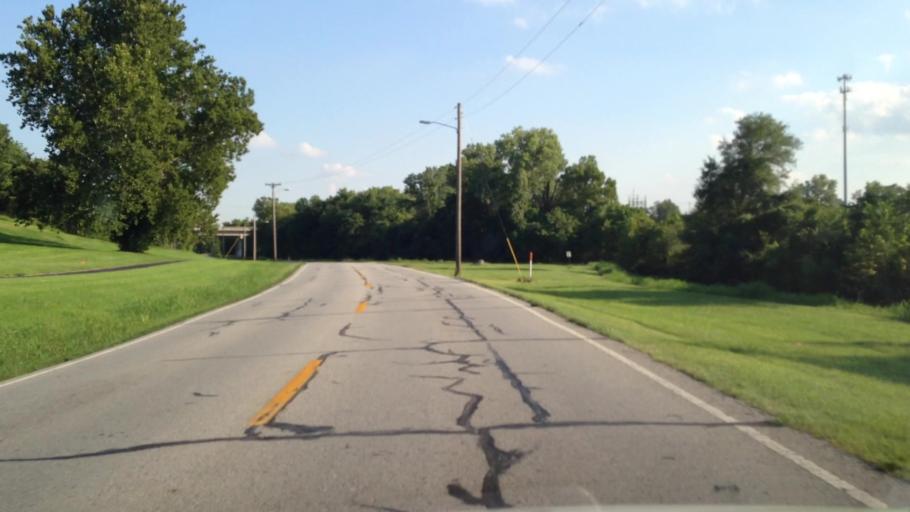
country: US
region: Missouri
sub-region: Jasper County
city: Joplin
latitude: 37.0941
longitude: -94.5107
